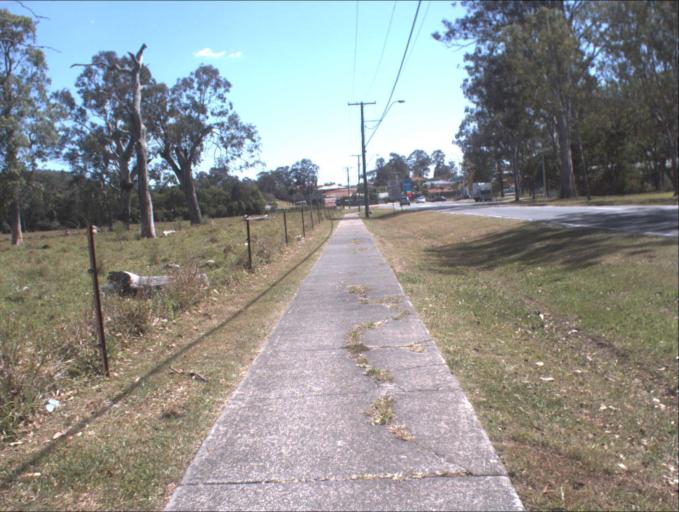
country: AU
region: Queensland
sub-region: Logan
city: Windaroo
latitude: -27.7550
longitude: 153.1864
